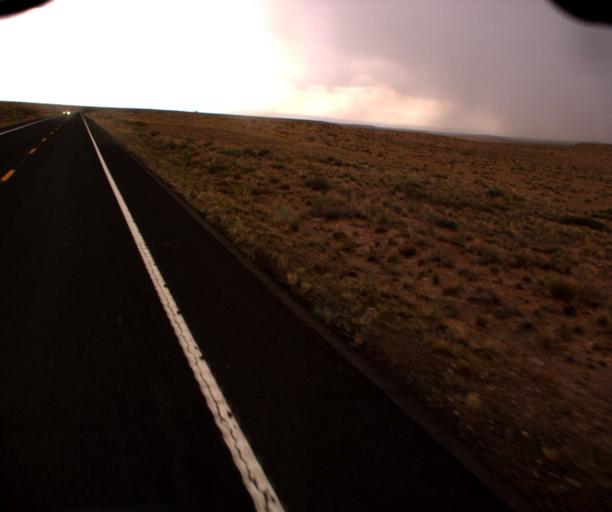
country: US
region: Arizona
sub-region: Coconino County
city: Tuba City
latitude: 36.1715
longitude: -111.0863
